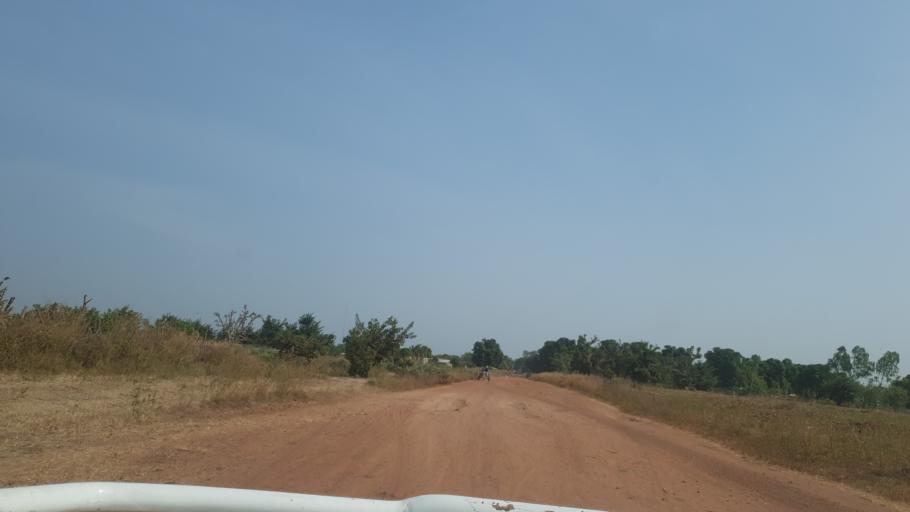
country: ML
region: Koulikoro
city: Dioila
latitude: 12.2221
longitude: -6.2119
